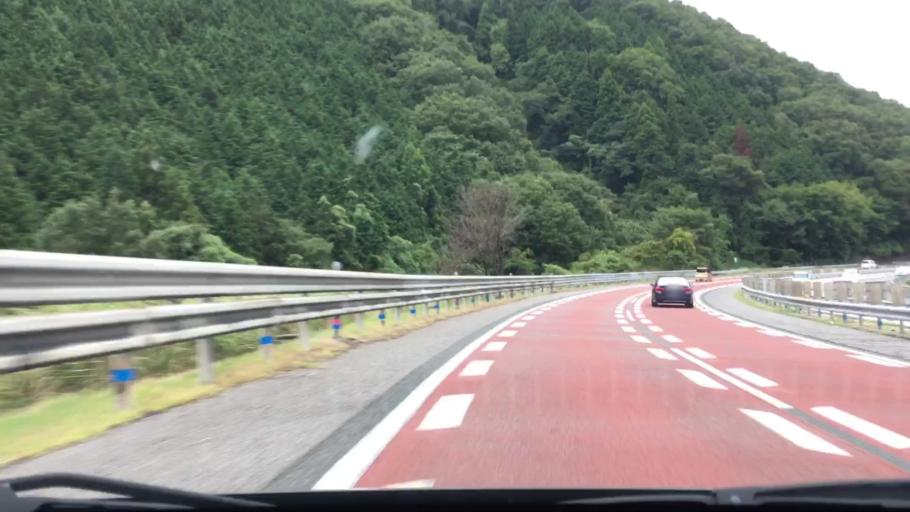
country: JP
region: Hiroshima
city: Miyoshi
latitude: 34.7807
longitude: 132.8440
